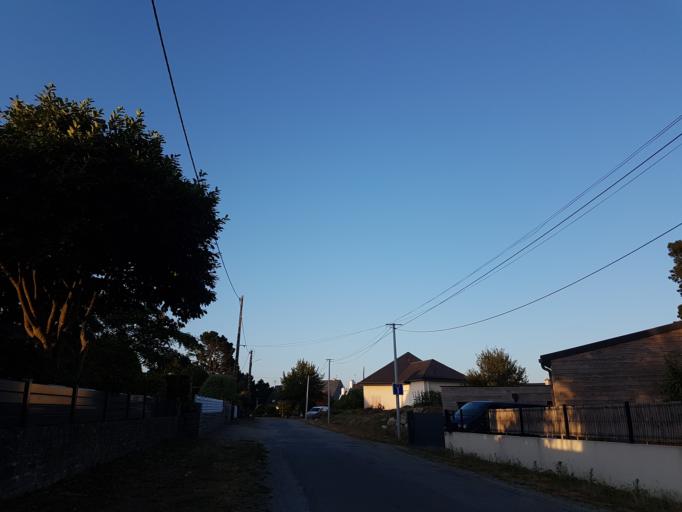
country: FR
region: Brittany
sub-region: Departement du Morbihan
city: Etel
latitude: 47.6810
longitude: -3.2032
